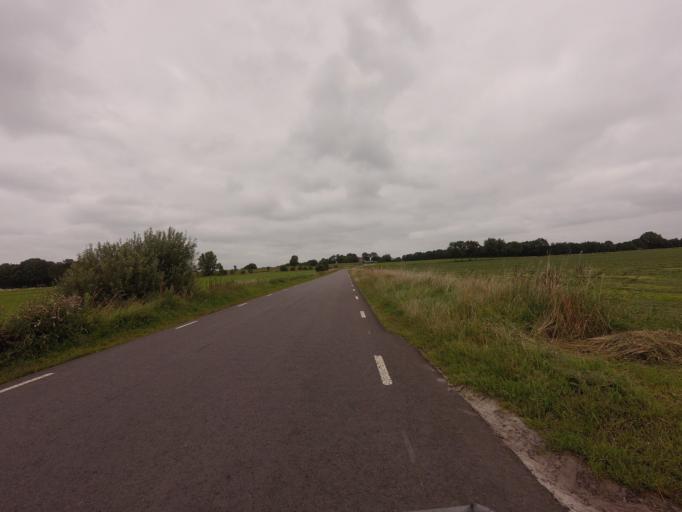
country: NL
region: Overijssel
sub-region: Gemeente Steenwijkerland
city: Steenwijkerwold
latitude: 52.7945
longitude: 6.0460
